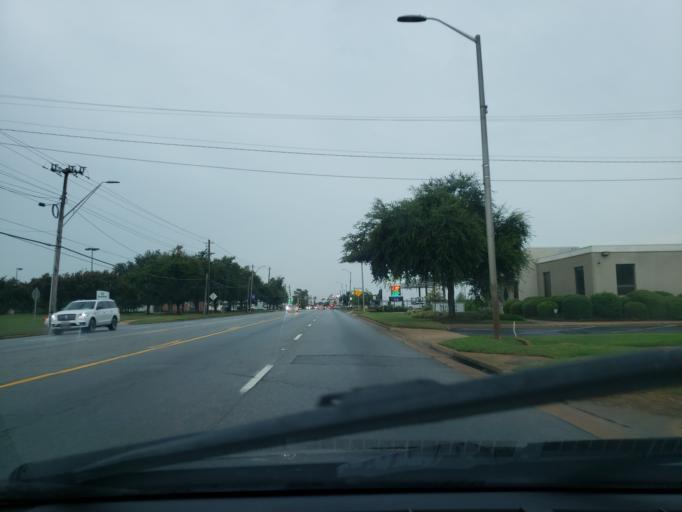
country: US
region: Georgia
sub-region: Dougherty County
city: Albany
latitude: 31.6037
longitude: -84.2046
